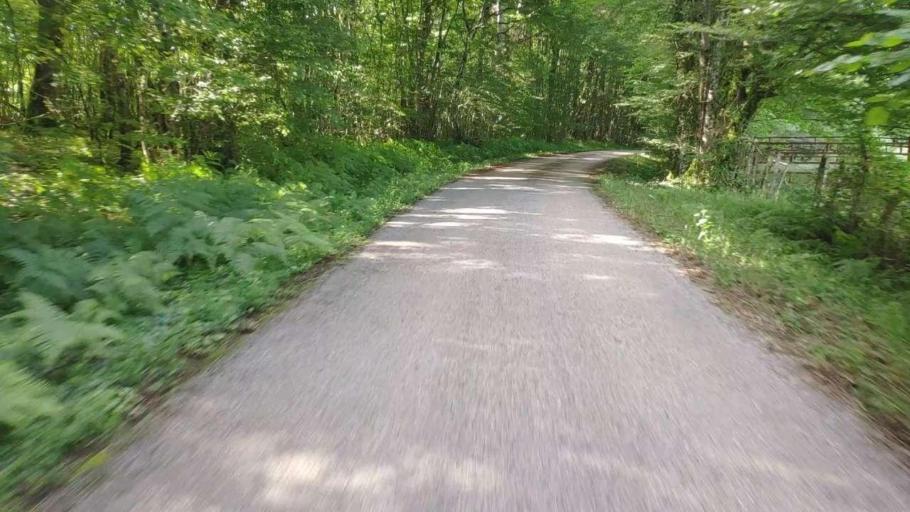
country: FR
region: Franche-Comte
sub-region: Departement du Jura
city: Bletterans
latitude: 46.8062
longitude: 5.4963
